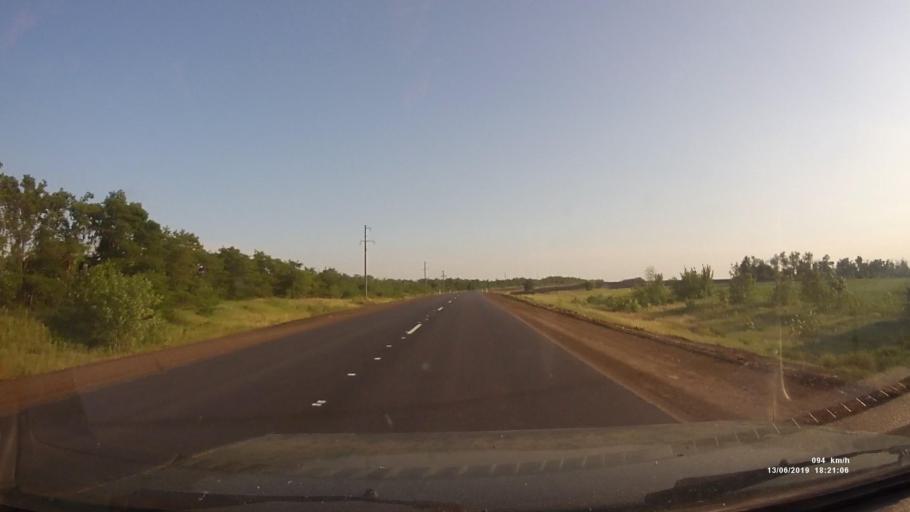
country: RU
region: Rostov
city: Kazanskaya
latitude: 49.8749
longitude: 41.2940
